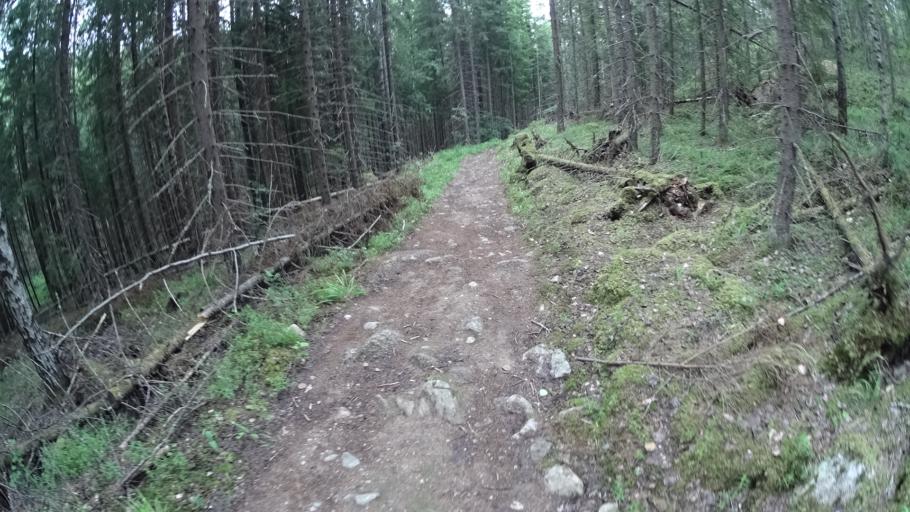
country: FI
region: Southern Savonia
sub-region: Mikkeli
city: Maentyharju
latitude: 61.1804
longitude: 26.8960
